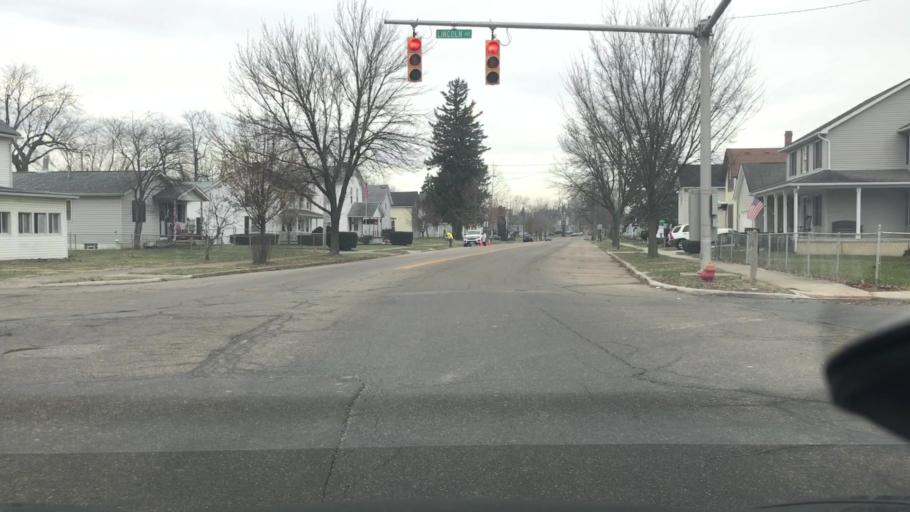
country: US
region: Ohio
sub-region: Madison County
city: London
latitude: 39.8804
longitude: -83.4404
